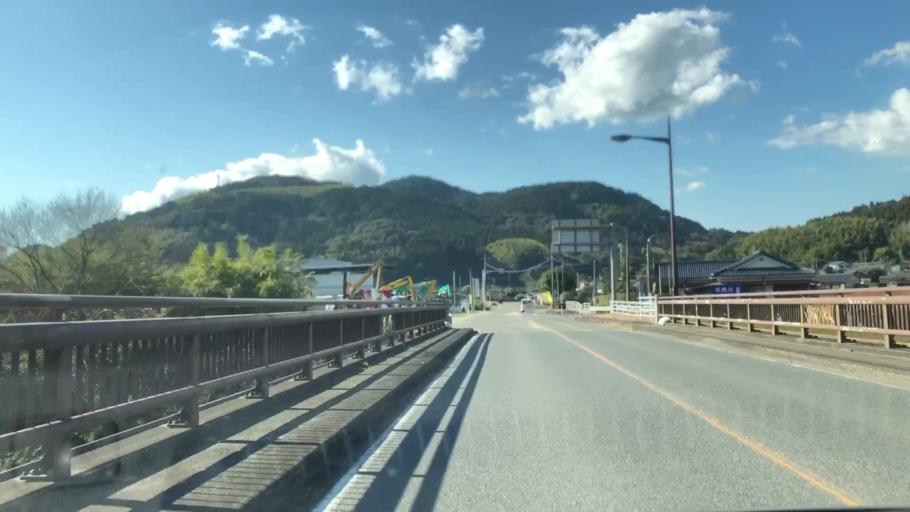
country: JP
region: Kagoshima
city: Satsumasendai
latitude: 31.8682
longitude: 130.4297
